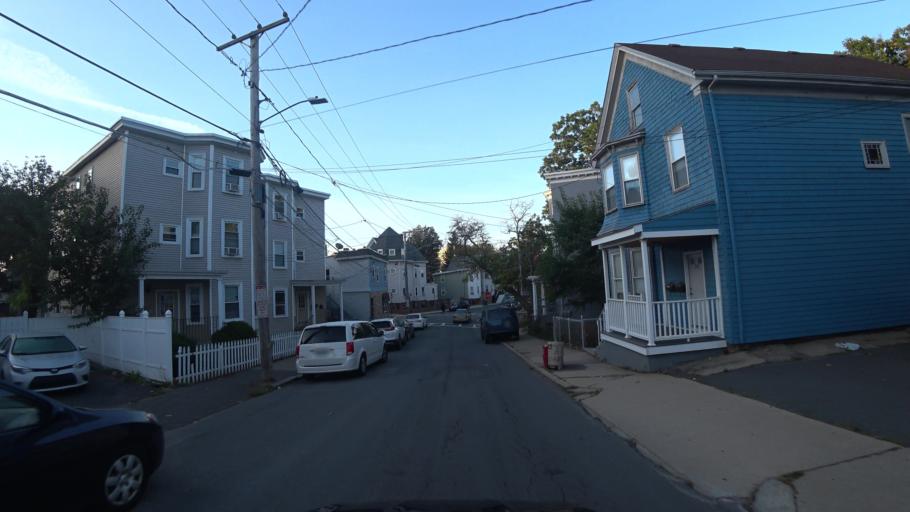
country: US
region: Massachusetts
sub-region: Suffolk County
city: Chelsea
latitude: 42.4019
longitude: -71.0365
